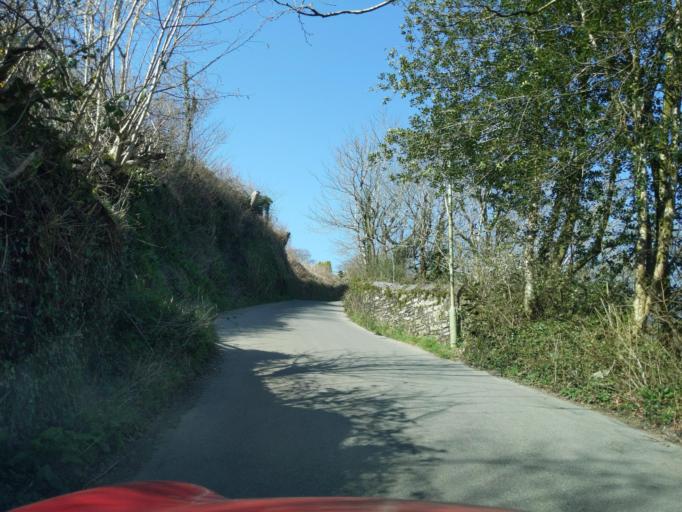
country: GB
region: England
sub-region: Devon
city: Horrabridge
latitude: 50.4757
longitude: -4.1312
